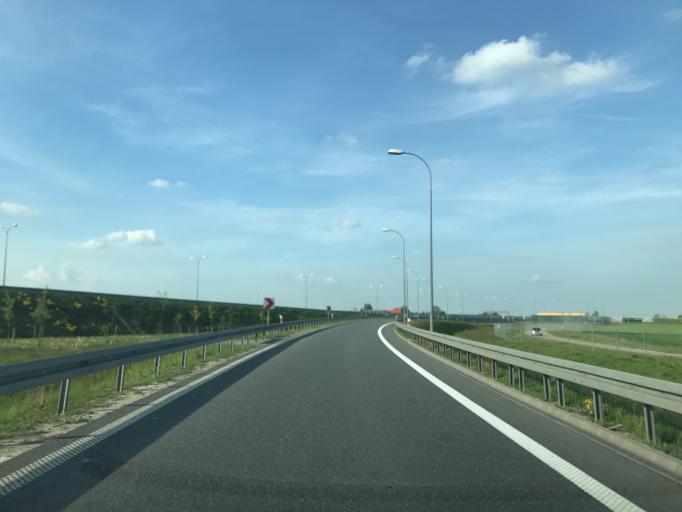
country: PL
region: Kujawsko-Pomorskie
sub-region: Powiat torunski
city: Lubicz Dolny
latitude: 53.0902
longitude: 18.7512
